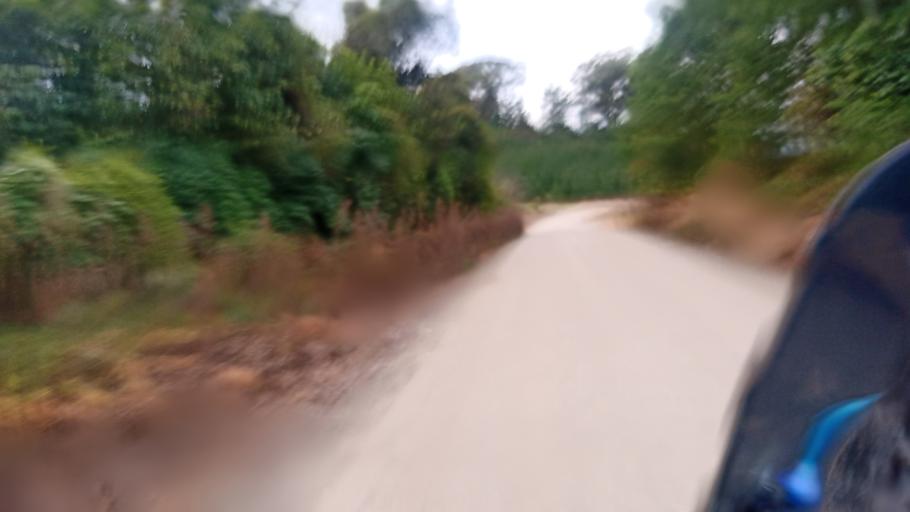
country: NZ
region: Gisborne
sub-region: Gisborne District
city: Gisborne
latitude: -38.3803
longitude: 177.9632
